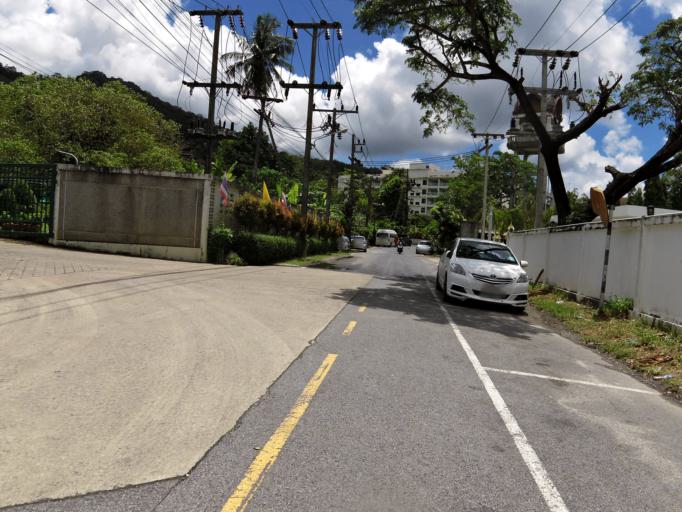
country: TH
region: Phuket
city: Ban Karon
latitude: 7.8558
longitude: 98.2943
